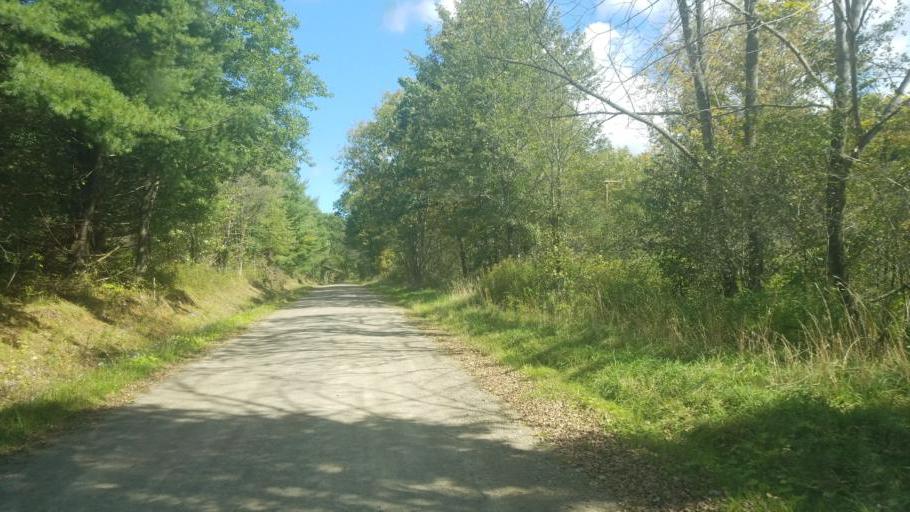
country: US
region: New York
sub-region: Allegany County
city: Cuba
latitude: 42.1869
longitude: -78.3302
